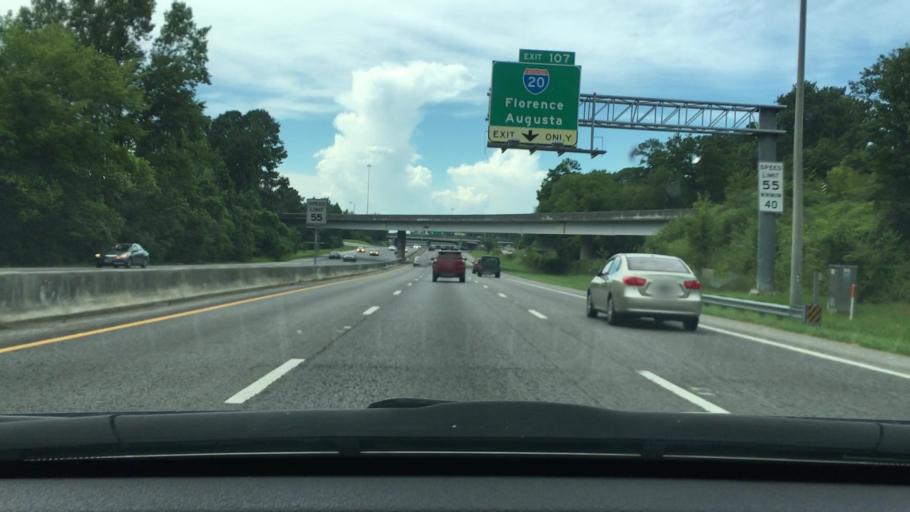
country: US
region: South Carolina
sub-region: Lexington County
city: Saint Andrews
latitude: 34.0245
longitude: -81.0981
